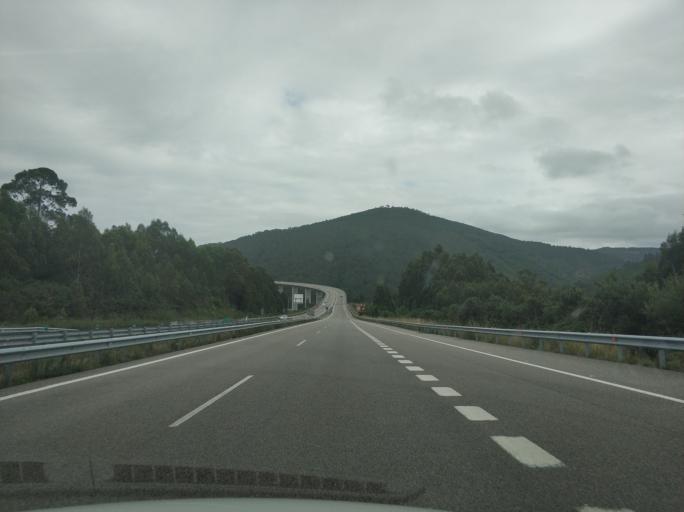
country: ES
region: Asturias
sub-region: Province of Asturias
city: Cudillero
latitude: 43.5565
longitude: -6.2026
